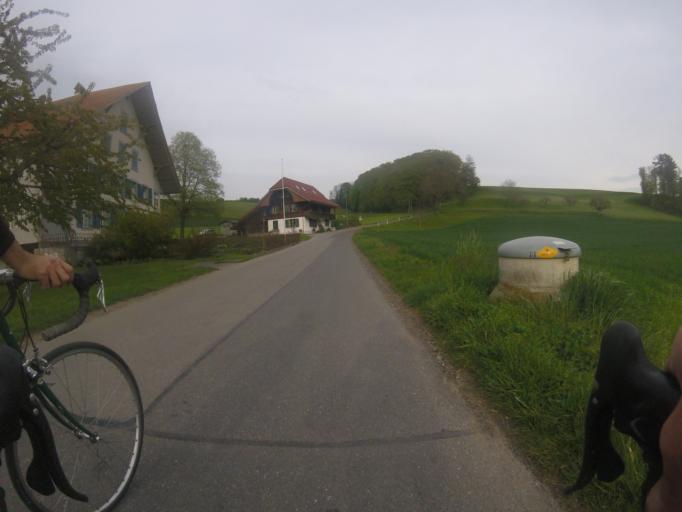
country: CH
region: Bern
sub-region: Bern-Mittelland District
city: Niederwichtrach
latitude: 46.8422
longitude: 7.5861
